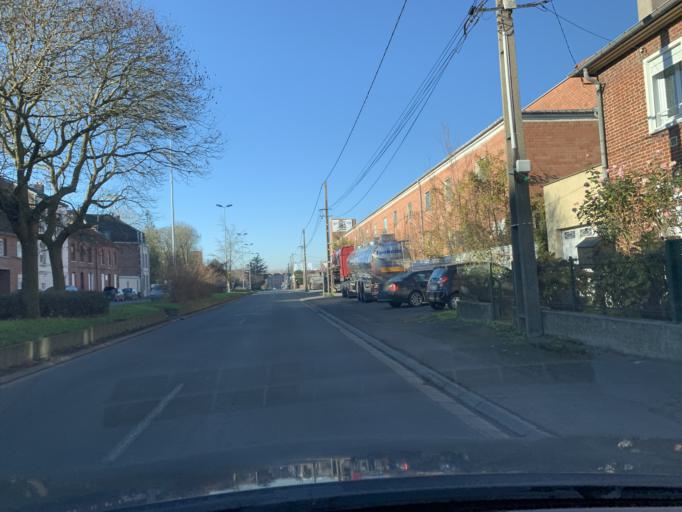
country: FR
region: Nord-Pas-de-Calais
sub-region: Departement du Nord
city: Cambrai
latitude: 50.1814
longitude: 3.2394
